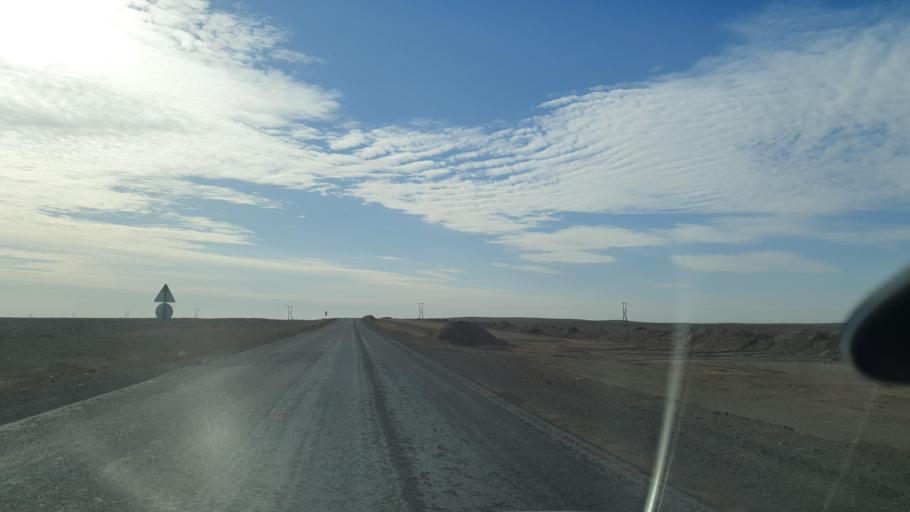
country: KZ
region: Qaraghandy
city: Saryshaghan
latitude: 45.9800
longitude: 73.5585
